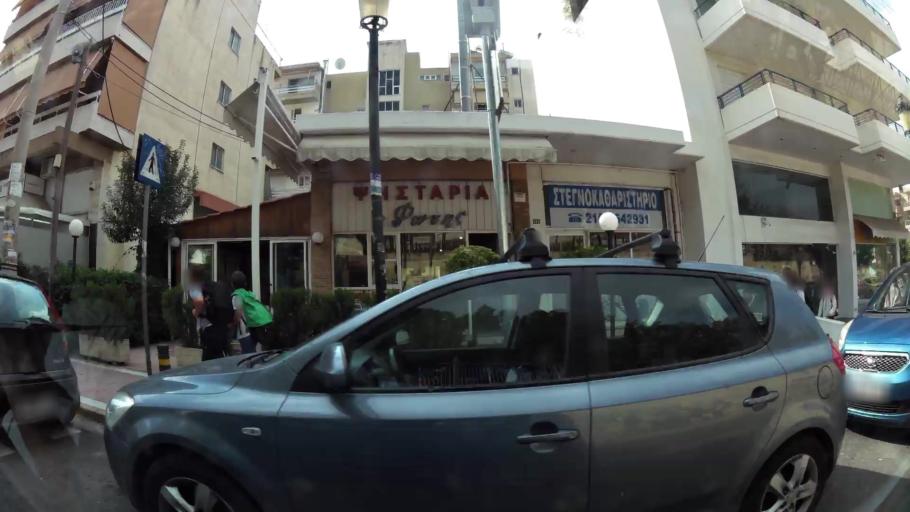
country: GR
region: Attica
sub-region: Nomarchia Athinas
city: Cholargos
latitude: 37.9980
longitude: 23.8072
